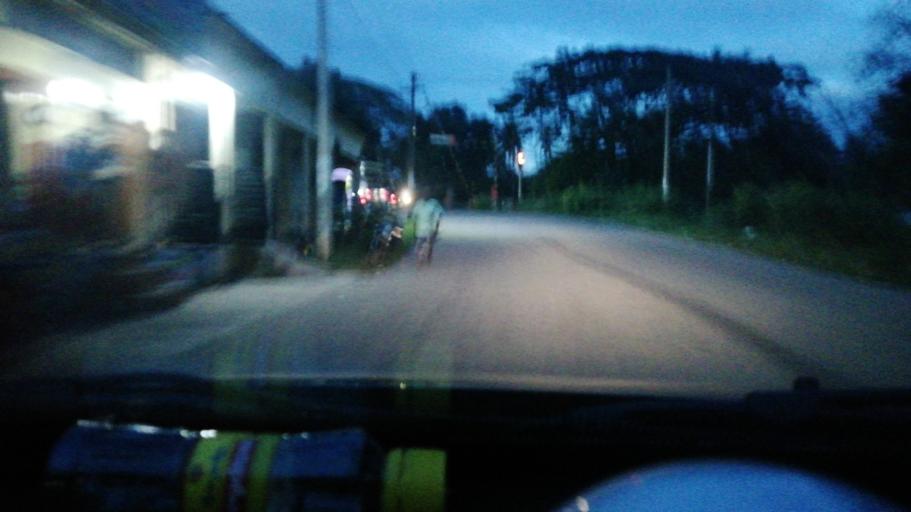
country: IN
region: Kerala
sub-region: Thiruvananthapuram
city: Paravur
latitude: 8.8126
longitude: 76.6747
